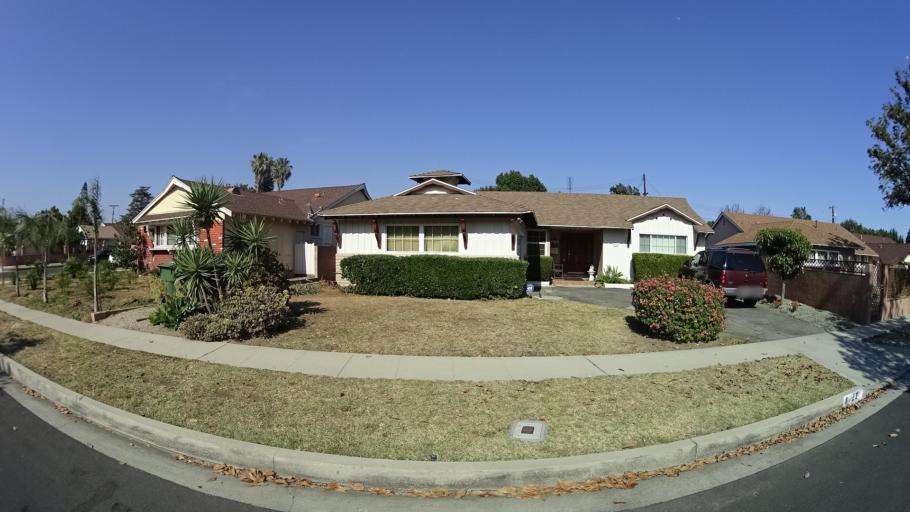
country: US
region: California
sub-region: Los Angeles County
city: Van Nuys
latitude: 34.2184
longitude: -118.4276
